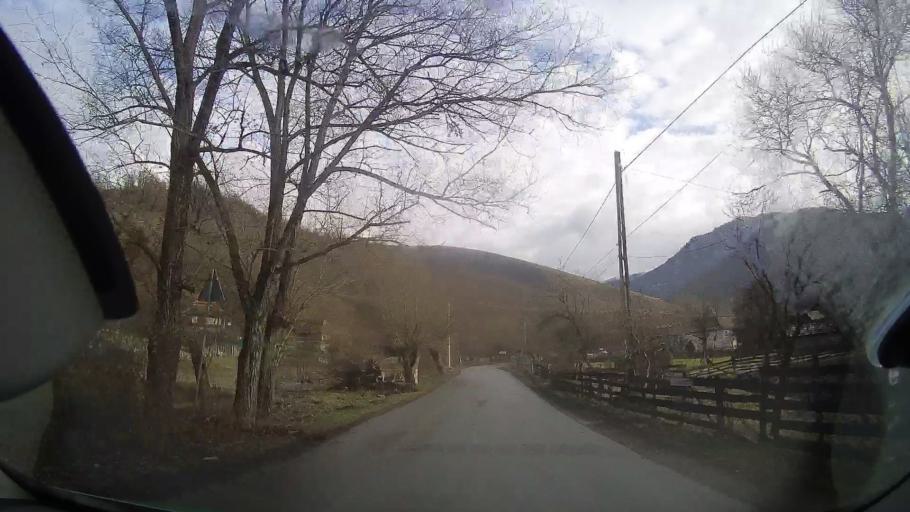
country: RO
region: Alba
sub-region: Comuna Ocolis
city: Ocolis
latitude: 46.4751
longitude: 23.4684
